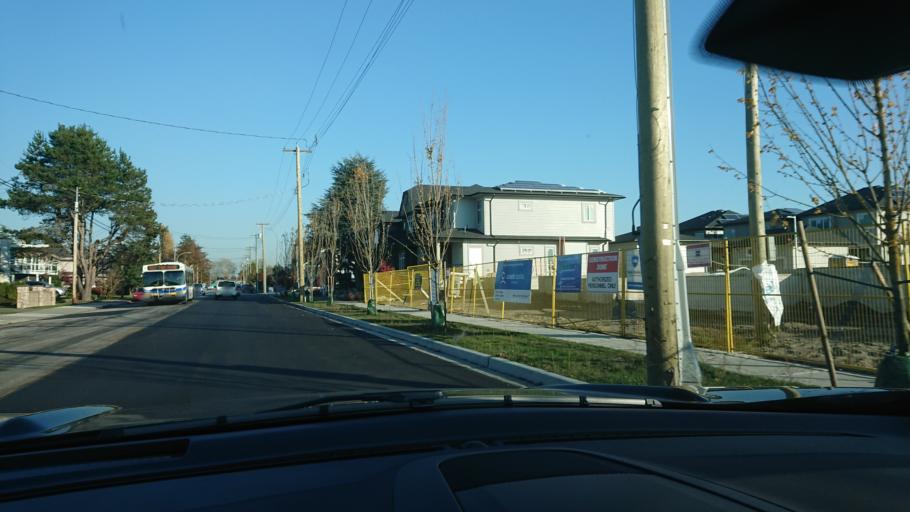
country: CA
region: British Columbia
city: Richmond
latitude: 49.1251
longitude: -123.1635
